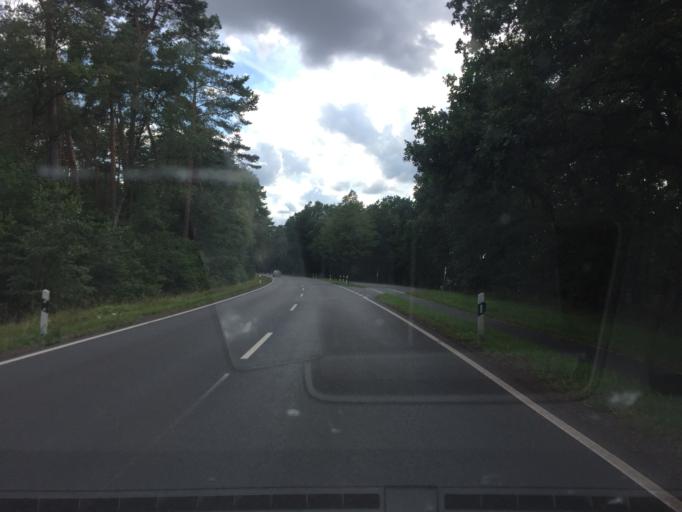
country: DE
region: Lower Saxony
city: Heemsen
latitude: 52.7349
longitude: 9.2954
